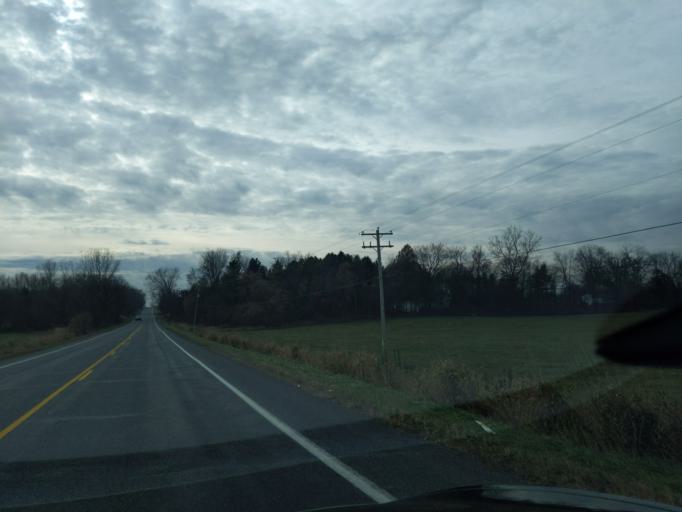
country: US
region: Michigan
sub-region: Ingham County
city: Holt
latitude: 42.6053
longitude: -84.5231
